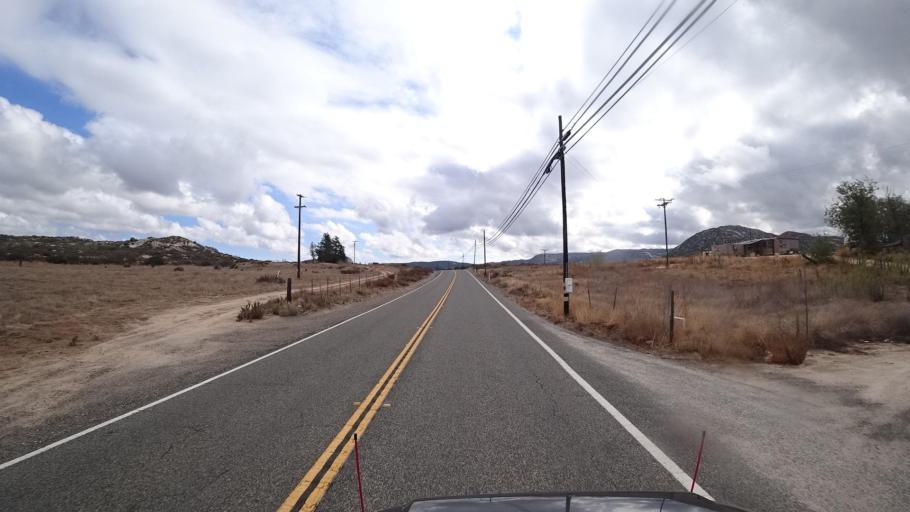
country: US
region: California
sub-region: San Diego County
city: Campo
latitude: 32.6301
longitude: -116.4413
